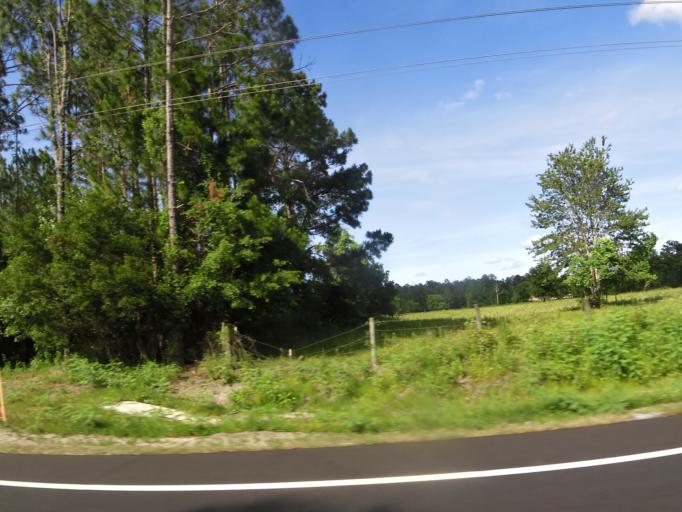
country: US
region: Florida
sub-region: Nassau County
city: Callahan
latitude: 30.6068
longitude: -81.8719
